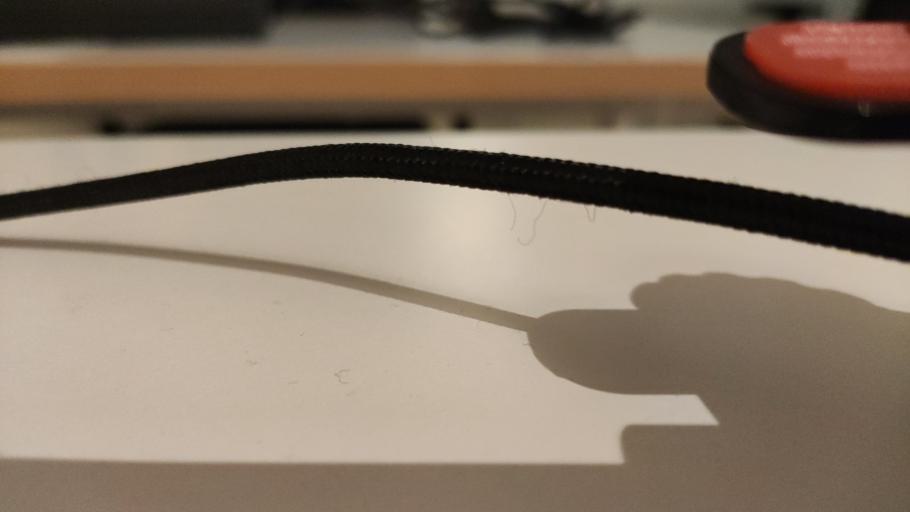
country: RU
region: Moskovskaya
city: Novoye
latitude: 55.6309
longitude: 38.9418
